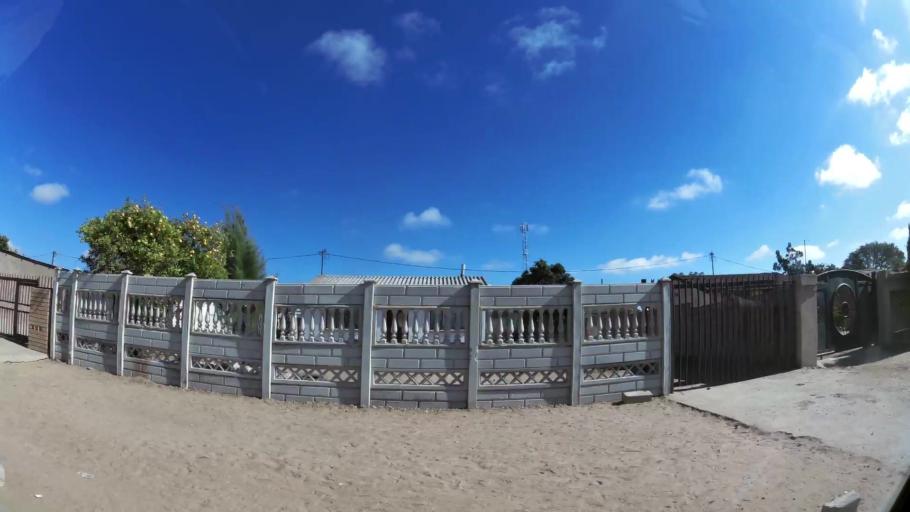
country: ZA
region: Limpopo
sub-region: Capricorn District Municipality
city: Polokwane
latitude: -23.8641
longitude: 29.3910
